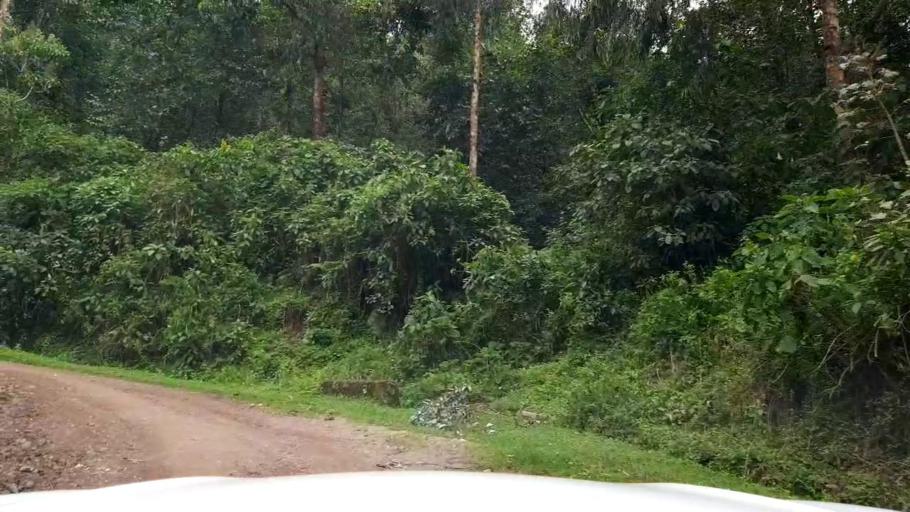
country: RW
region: Western Province
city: Gisenyi
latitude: -1.6542
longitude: 29.4156
